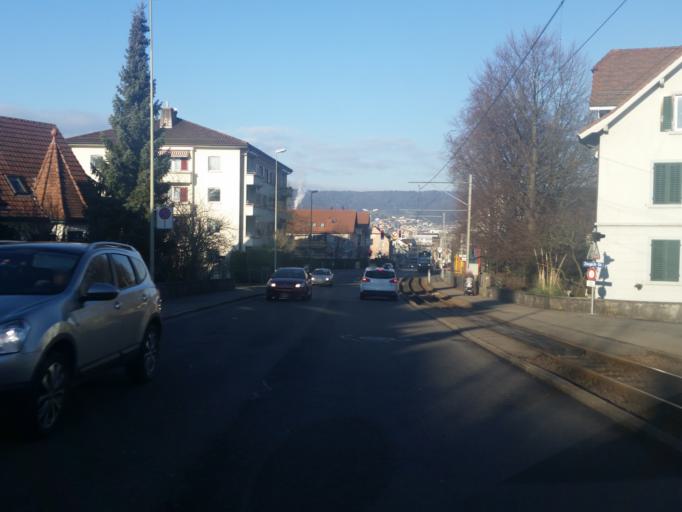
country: CH
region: Zurich
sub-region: Bezirk Dietikon
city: Dietikon / Kreuzacker
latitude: 47.3992
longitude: 8.3996
